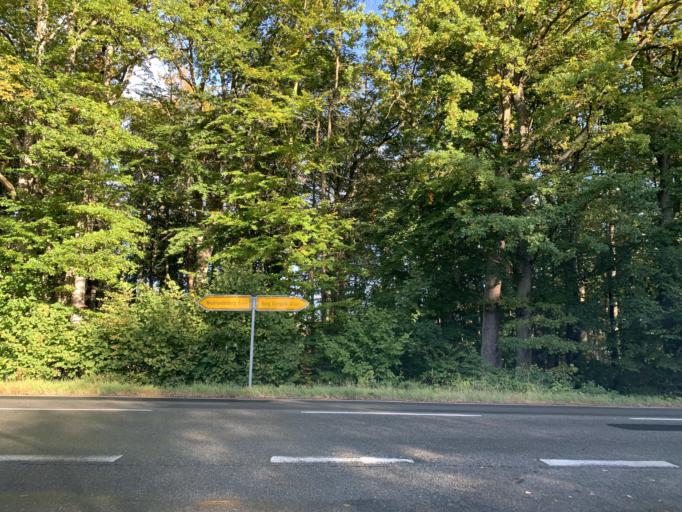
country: DE
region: Mecklenburg-Vorpommern
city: Burg Stargard
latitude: 53.5122
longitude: 13.2616
